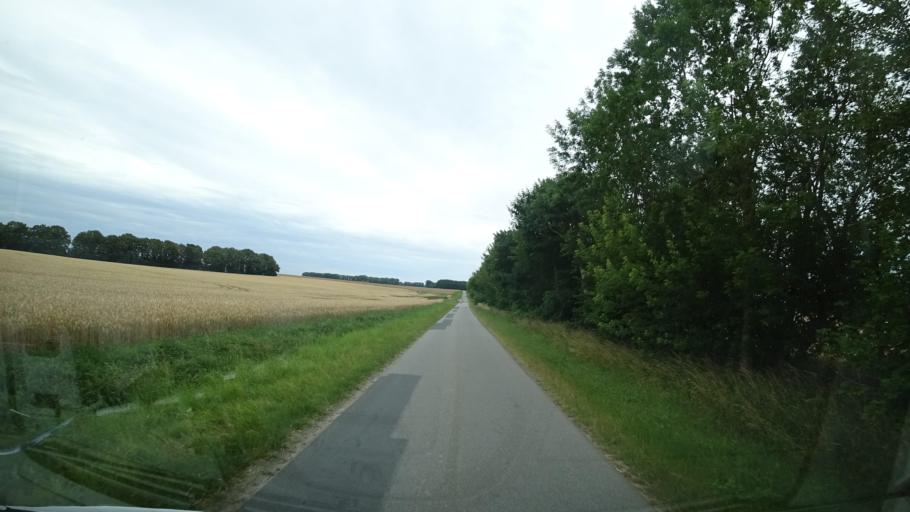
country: DE
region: Mecklenburg-Vorpommern
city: Rambin
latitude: 54.3198
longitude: 13.2033
